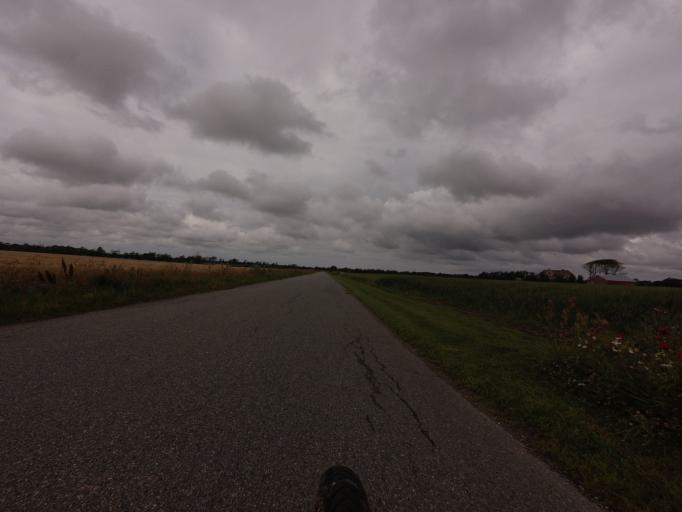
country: DK
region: North Denmark
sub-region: Bronderslev Kommune
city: Bronderslev
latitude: 57.3066
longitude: 9.8035
